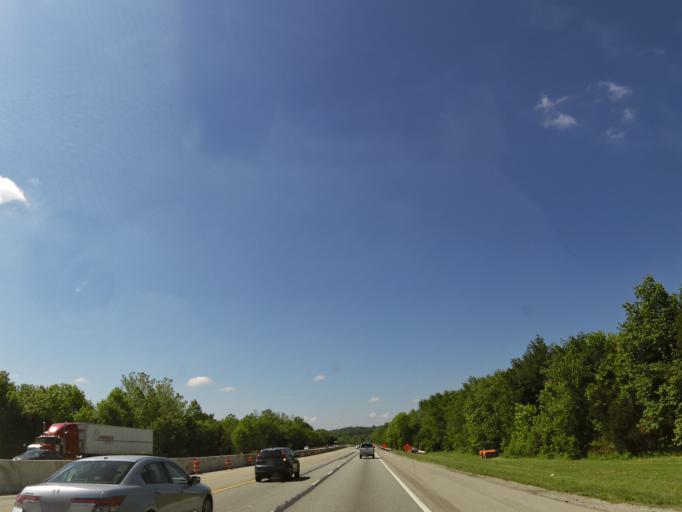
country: US
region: Kentucky
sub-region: Madison County
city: Berea
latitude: 37.4783
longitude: -84.3332
